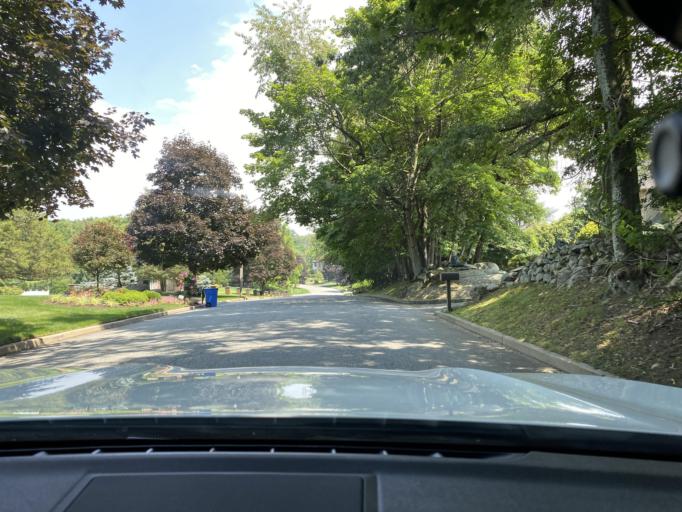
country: US
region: New York
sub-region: Rockland County
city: Airmont
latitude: 41.0889
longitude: -74.1247
